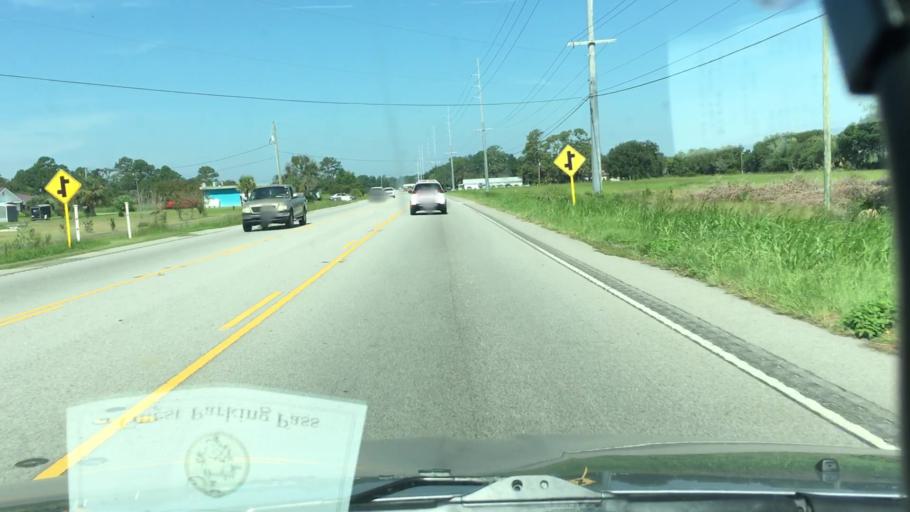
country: US
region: South Carolina
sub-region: Beaufort County
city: Beaufort
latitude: 32.3971
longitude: -80.6079
